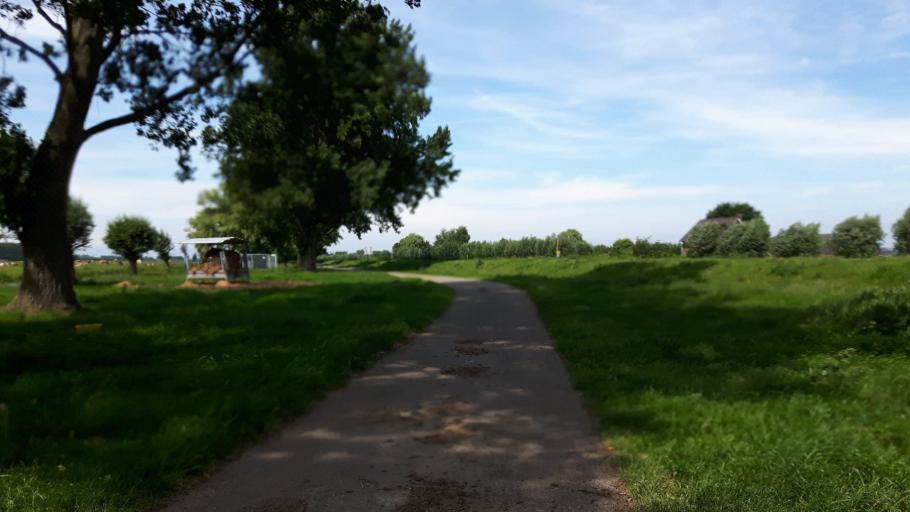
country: NL
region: South Holland
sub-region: Gemeente Nieuwkoop
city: Nieuwkoop
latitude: 52.1959
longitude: 4.7382
